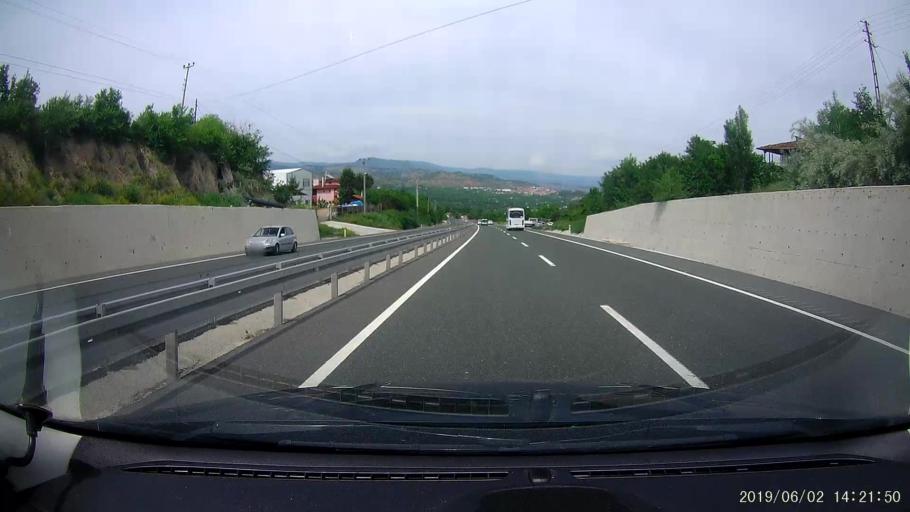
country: TR
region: Kastamonu
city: Tosya
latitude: 40.9842
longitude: 34.0072
